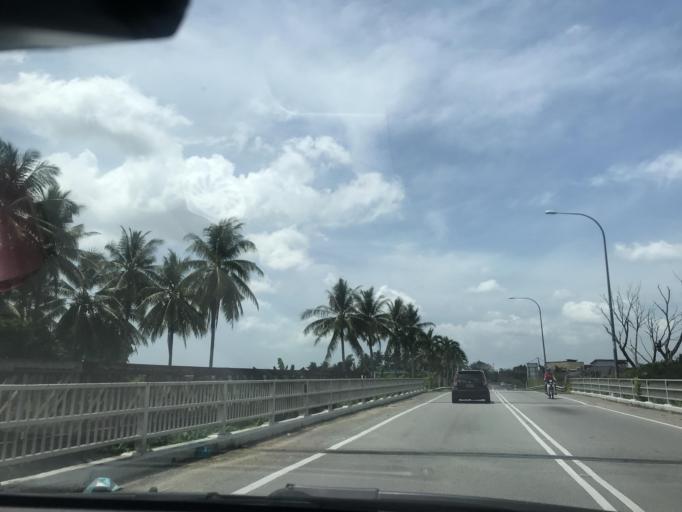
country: MY
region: Kelantan
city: Kota Bharu
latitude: 6.1534
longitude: 102.2053
